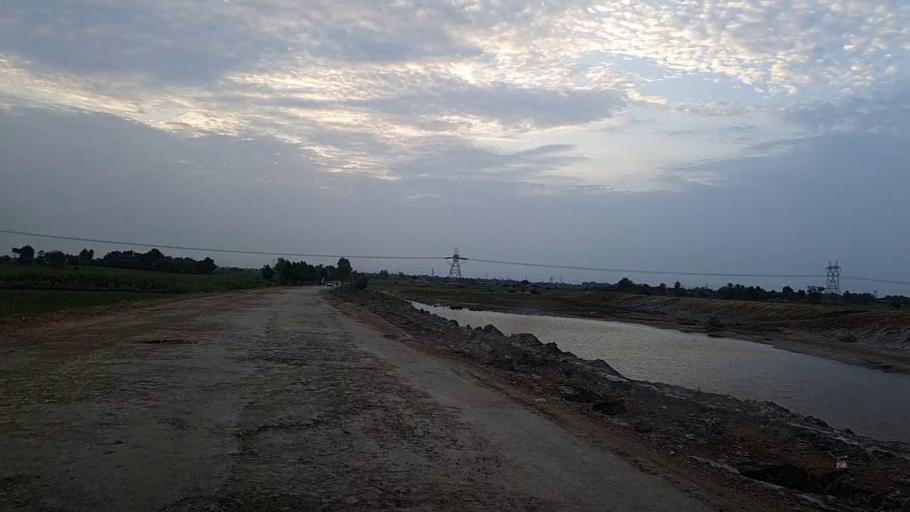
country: PK
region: Sindh
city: Naushahro Firoz
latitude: 26.8249
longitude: 68.1564
